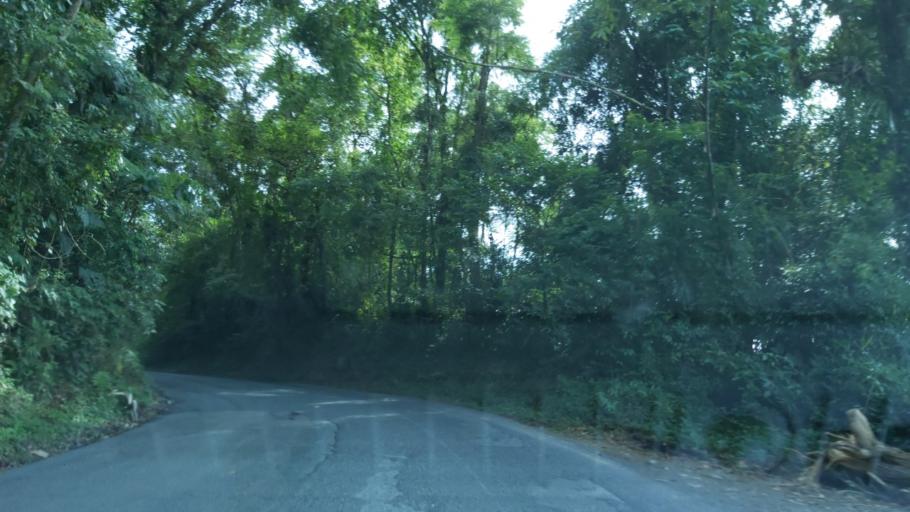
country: BR
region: Sao Paulo
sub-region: Juquia
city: Juquia
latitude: -24.0850
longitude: -47.6102
